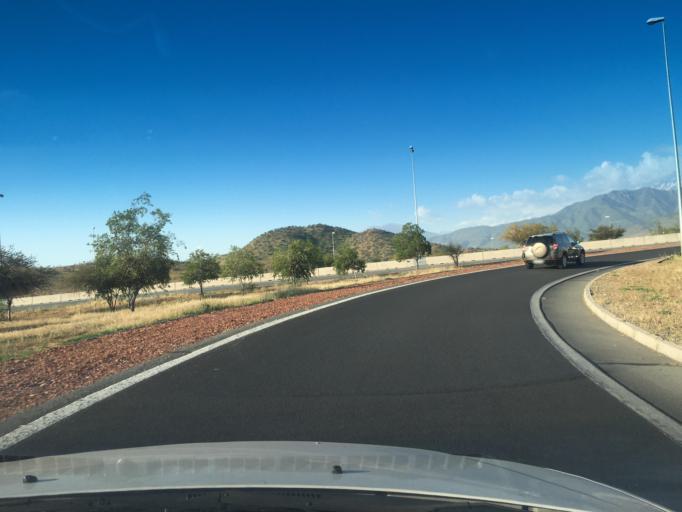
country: CL
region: Santiago Metropolitan
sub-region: Provincia de Chacabuco
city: Chicureo Abajo
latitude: -33.3009
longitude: -70.6618
